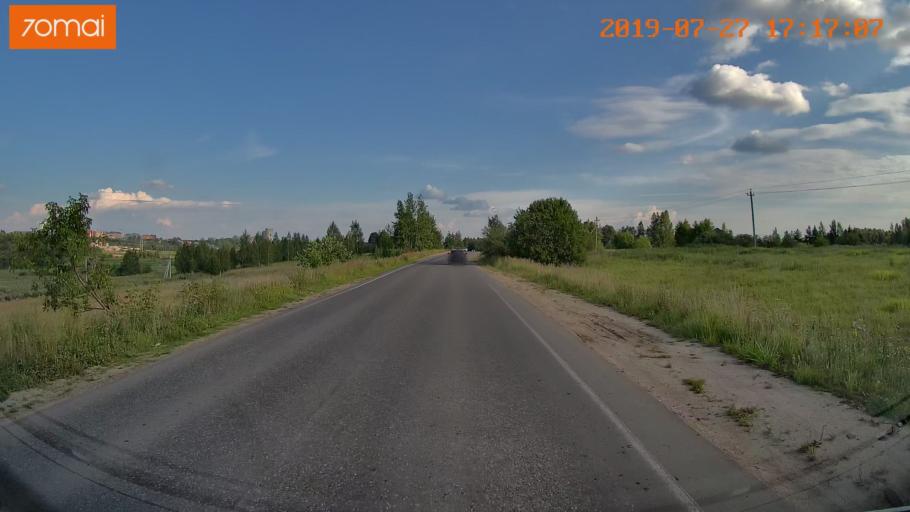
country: RU
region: Ivanovo
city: Novo-Talitsy
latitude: 57.0402
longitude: 40.8919
